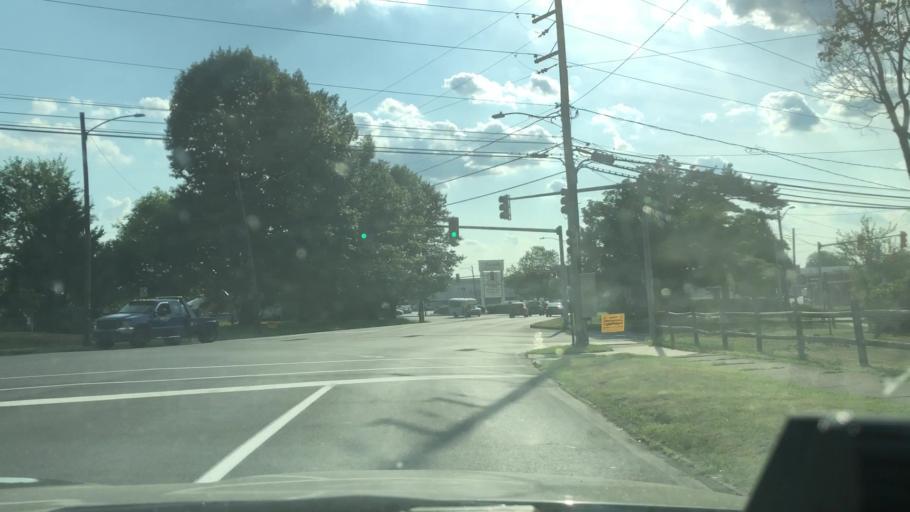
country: US
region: Pennsylvania
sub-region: Lehigh County
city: Fountain Hill
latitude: 40.6275
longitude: -75.4148
